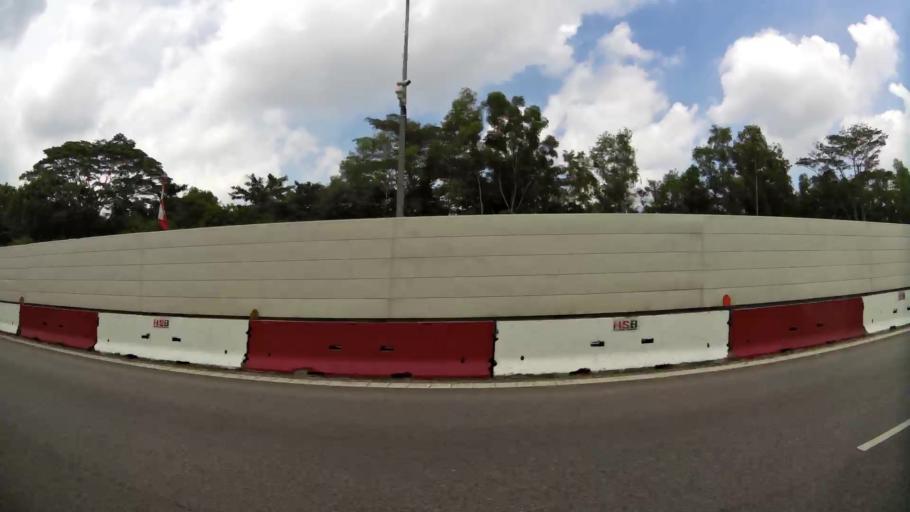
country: MY
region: Johor
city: Kampung Pasir Gudang Baru
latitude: 1.3776
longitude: 103.9115
